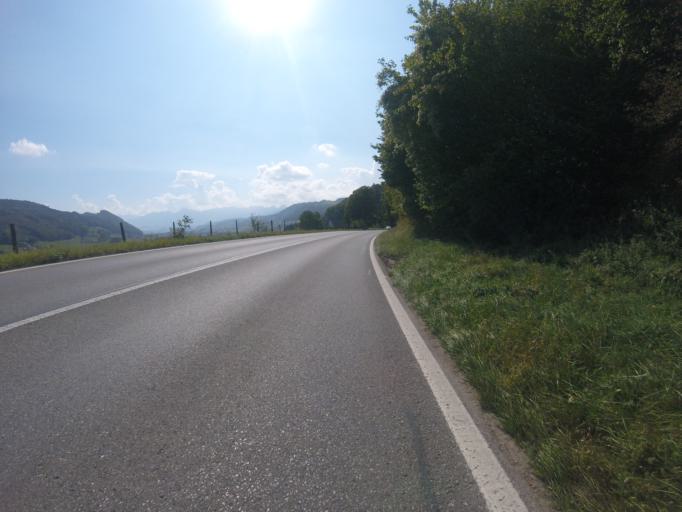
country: CH
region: Bern
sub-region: Bern-Mittelland District
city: Belp
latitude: 46.8801
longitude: 7.4950
